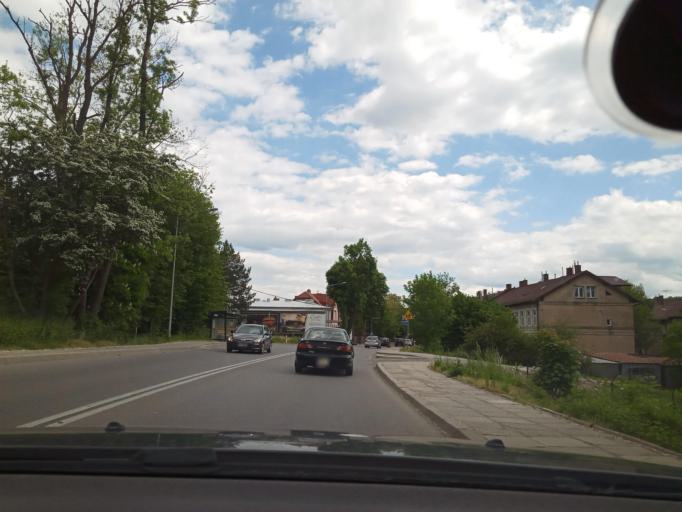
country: PL
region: Lesser Poland Voivodeship
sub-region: Powiat limanowski
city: Limanowa
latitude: 49.7249
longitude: 20.4023
